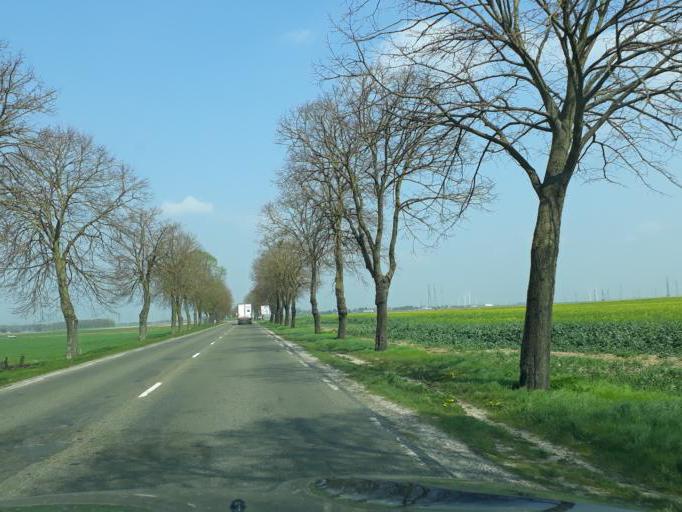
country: FR
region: Centre
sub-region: Departement du Loiret
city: Artenay
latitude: 48.0923
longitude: 1.8653
